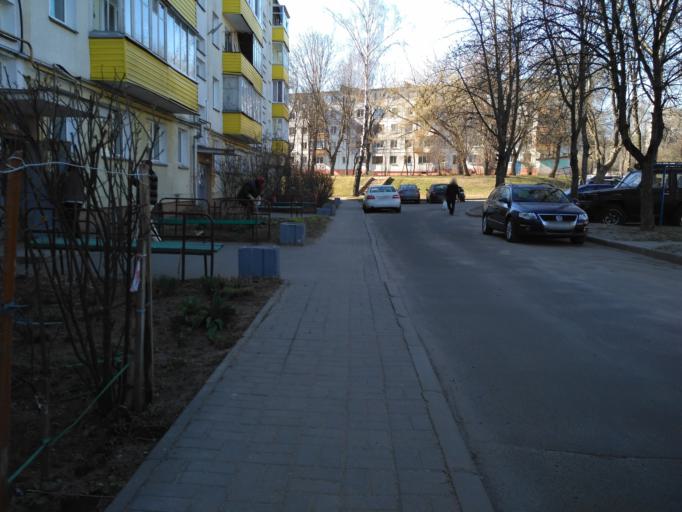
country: BY
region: Minsk
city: Minsk
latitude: 53.9036
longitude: 27.5089
